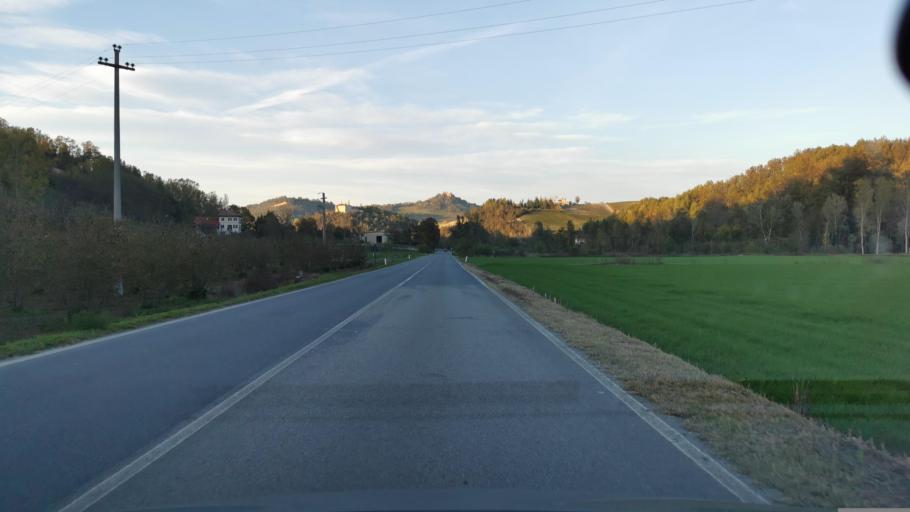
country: IT
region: Piedmont
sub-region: Provincia di Cuneo
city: Monchiero Borgonuovo
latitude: 44.5545
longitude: 7.9221
